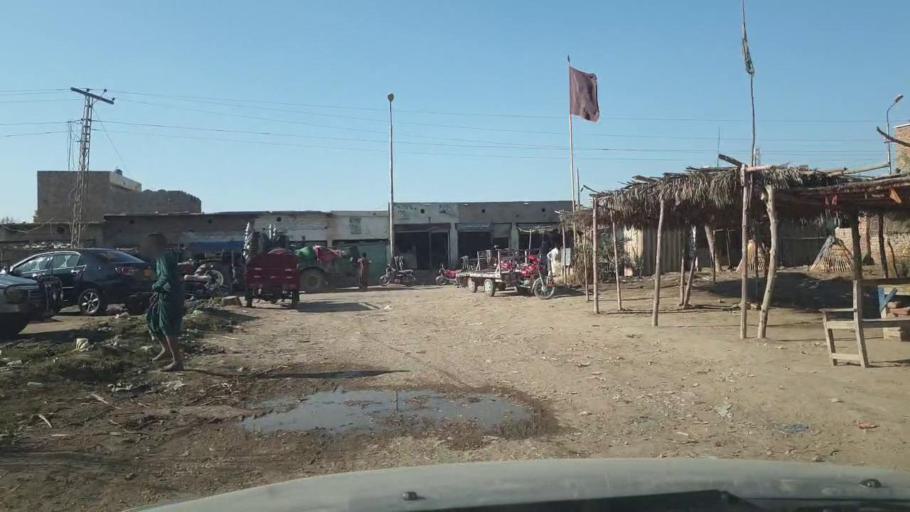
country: PK
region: Sindh
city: Ghotki
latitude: 28.0612
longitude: 69.3380
